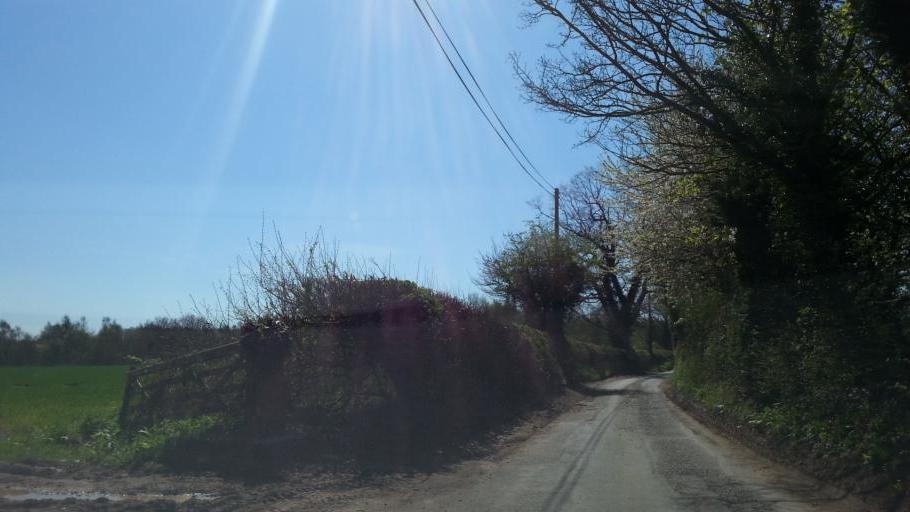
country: GB
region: England
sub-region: Staffordshire
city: Brewood
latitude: 52.6847
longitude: -2.1729
